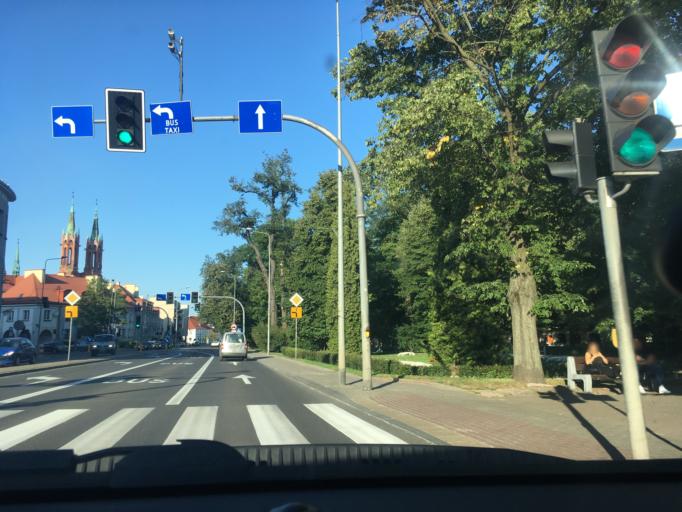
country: PL
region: Podlasie
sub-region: Bialystok
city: Bialystok
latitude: 53.1305
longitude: 23.1596
